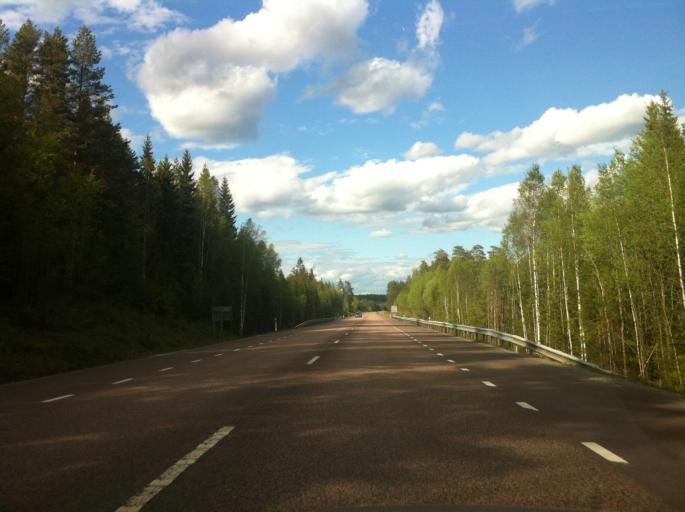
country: SE
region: Vaermland
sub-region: Filipstads Kommun
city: Filipstad
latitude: 59.7150
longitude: 14.1928
